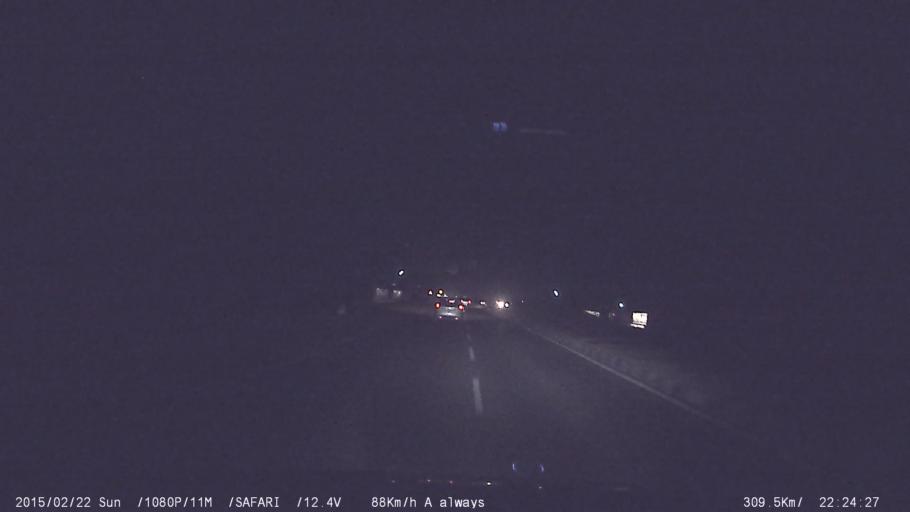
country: IN
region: Tamil Nadu
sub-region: Namakkal
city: Mohanur
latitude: 11.0374
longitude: 78.0607
